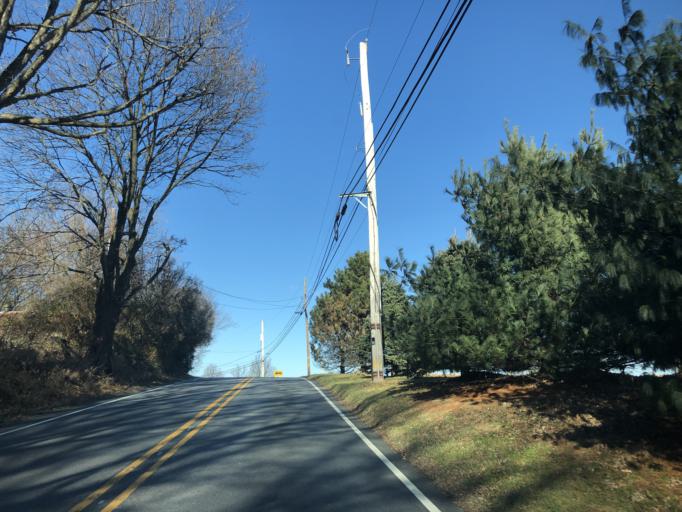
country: US
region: Pennsylvania
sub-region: Chester County
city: South Coatesville
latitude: 39.9442
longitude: -75.8347
